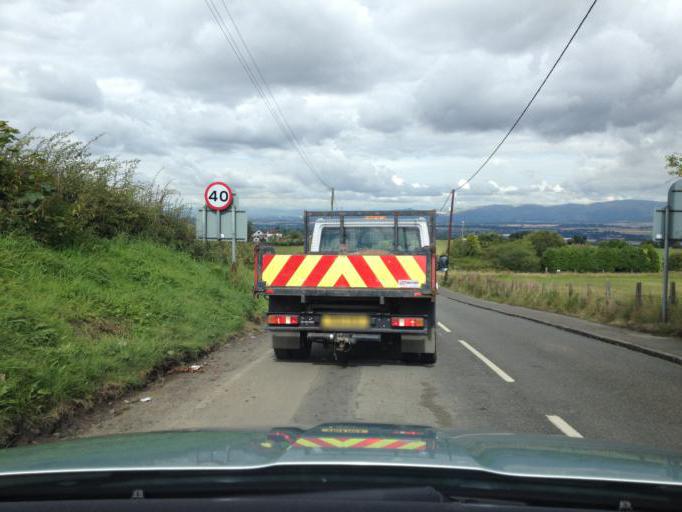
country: GB
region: Scotland
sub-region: Falkirk
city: Falkirk
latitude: 55.9692
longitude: -3.7557
